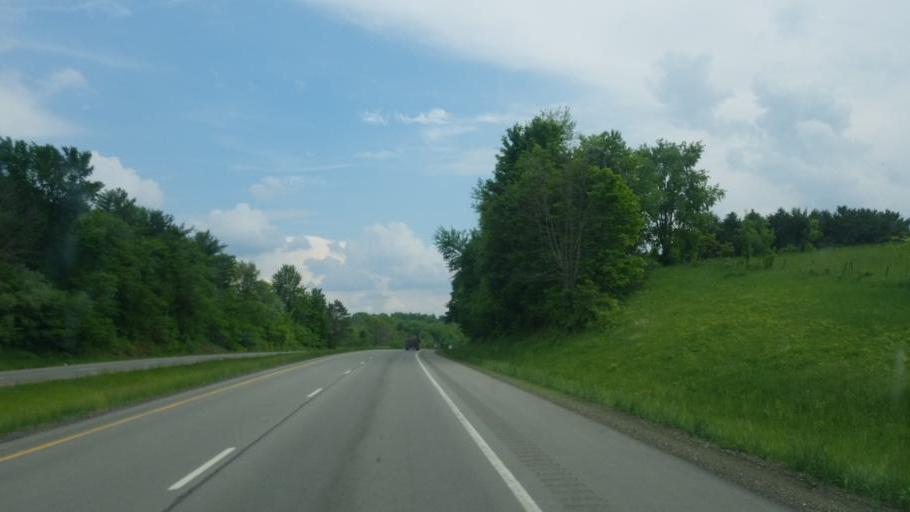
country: US
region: Ohio
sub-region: Sandusky County
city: Bellville
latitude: 40.6547
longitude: -82.5132
